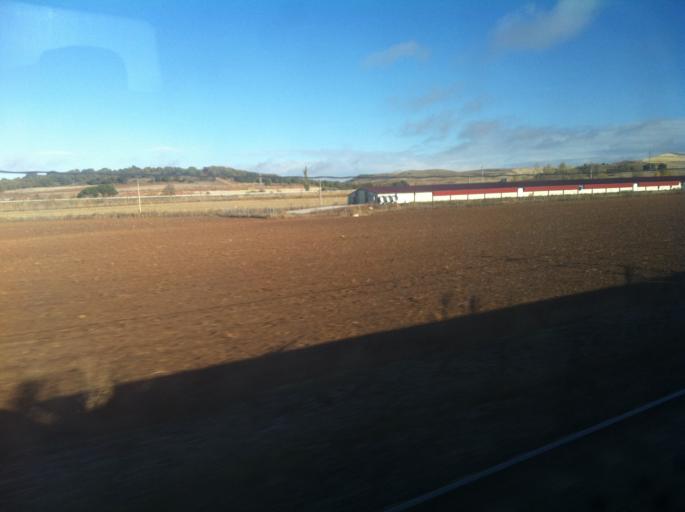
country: ES
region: Castille and Leon
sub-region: Provincia de Burgos
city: Estepar
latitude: 42.2767
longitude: -3.8836
